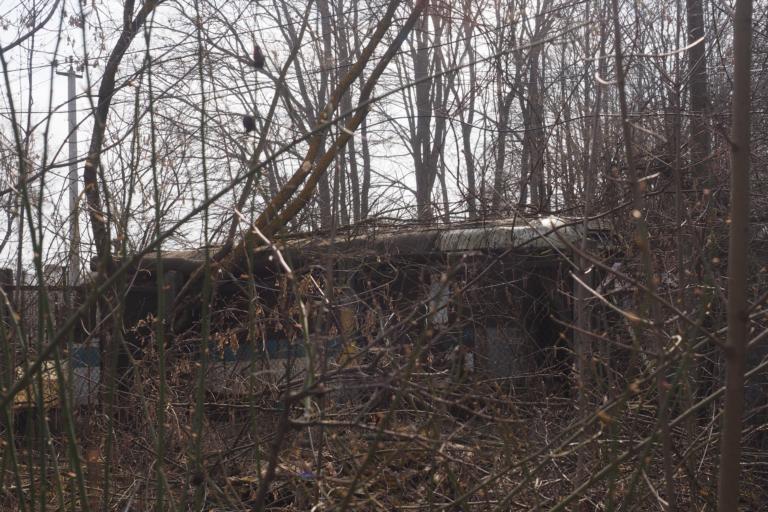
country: RU
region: Moskovskaya
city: Bronnitsy
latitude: 55.3912
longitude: 38.3508
